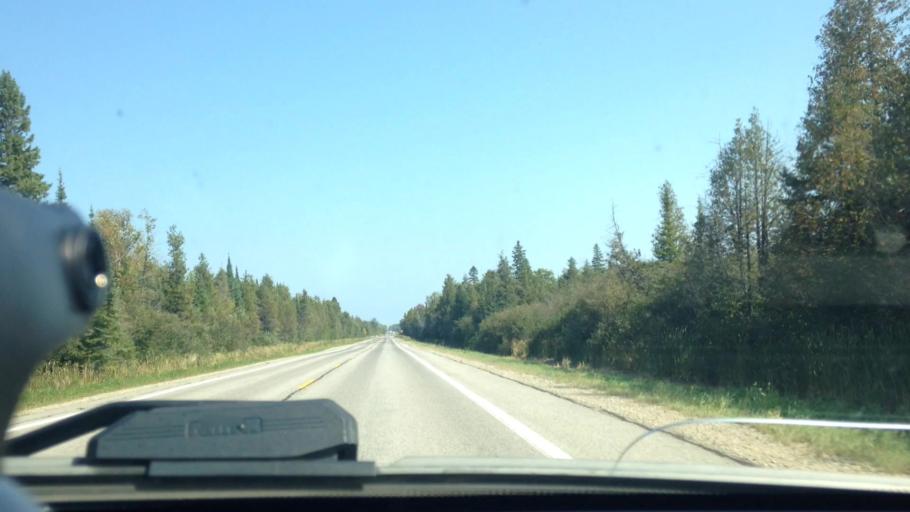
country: US
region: Michigan
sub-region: Luce County
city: Newberry
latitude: 46.3035
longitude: -85.4030
